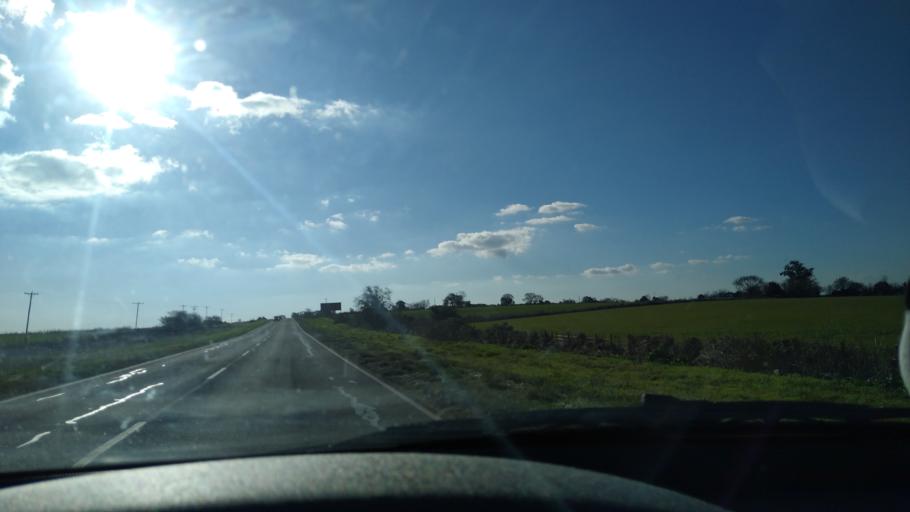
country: AR
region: Entre Rios
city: Diamante
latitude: -32.1104
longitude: -60.5771
